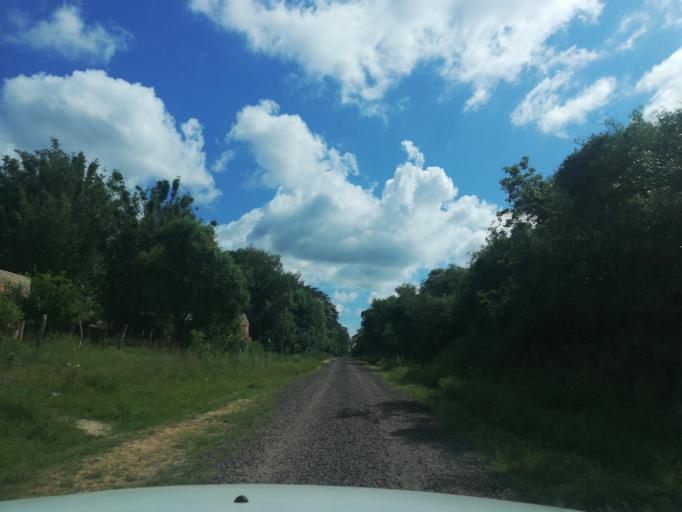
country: AR
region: Corrientes
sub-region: Departamento de San Miguel
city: San Miguel
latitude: -27.9882
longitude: -57.5441
